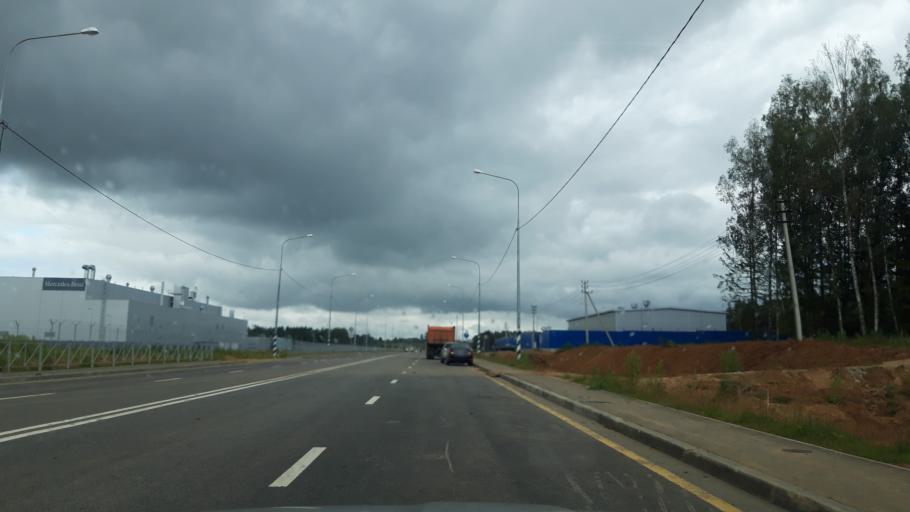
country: RU
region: Moskovskaya
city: Lozhki
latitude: 56.0823
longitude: 37.0882
